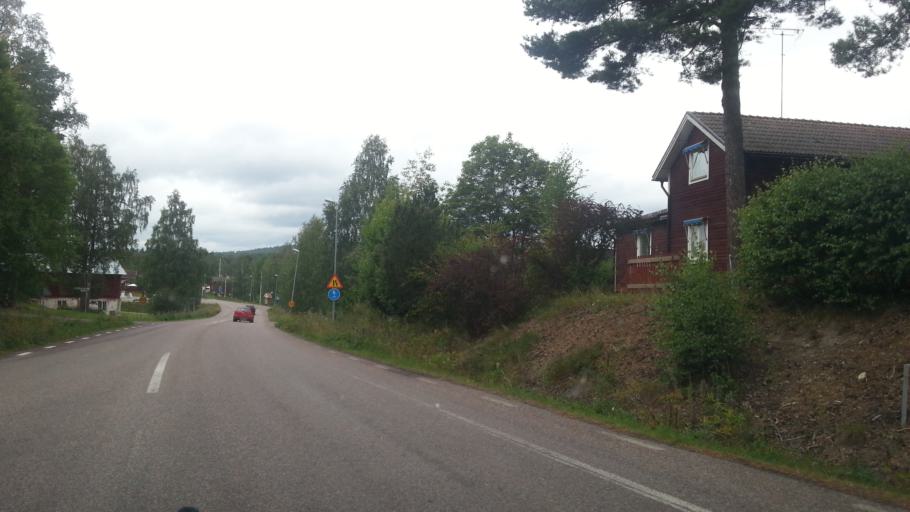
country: SE
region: Dalarna
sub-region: Faluns Kommun
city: Svardsjo
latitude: 60.6530
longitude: 15.7854
